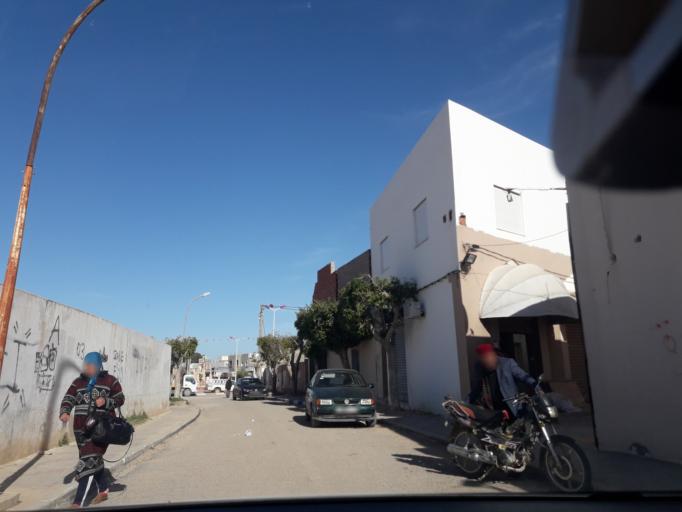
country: TN
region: Safaqis
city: Sfax
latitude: 34.7397
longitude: 10.5281
